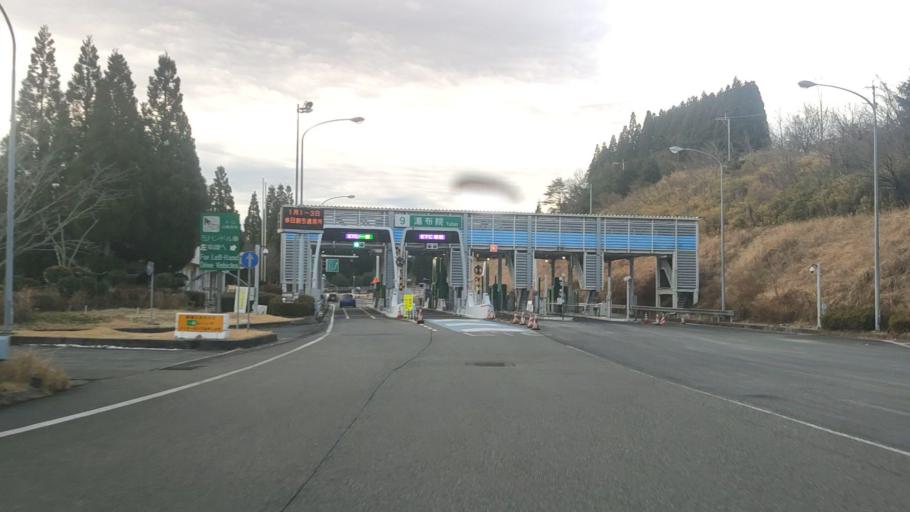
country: JP
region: Oita
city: Beppu
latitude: 33.2599
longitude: 131.3282
